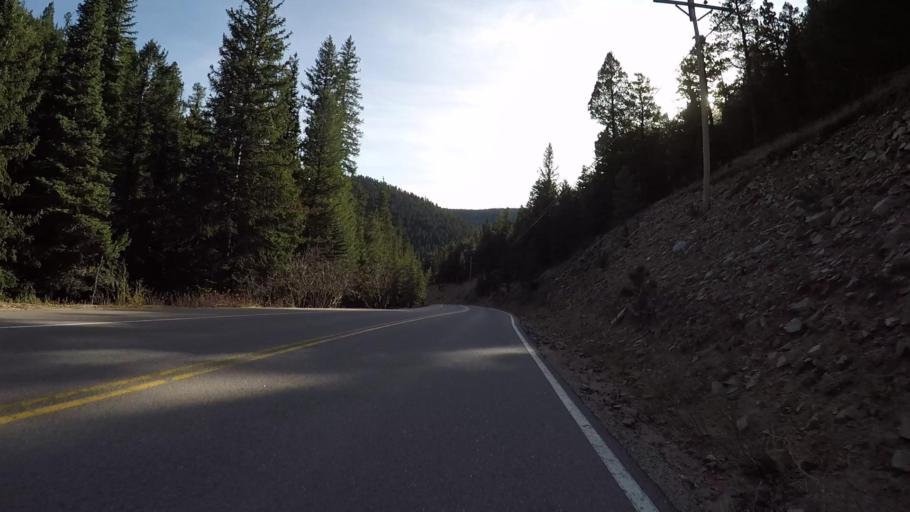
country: US
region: Colorado
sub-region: Boulder County
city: Nederland
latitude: 40.0590
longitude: -105.5008
